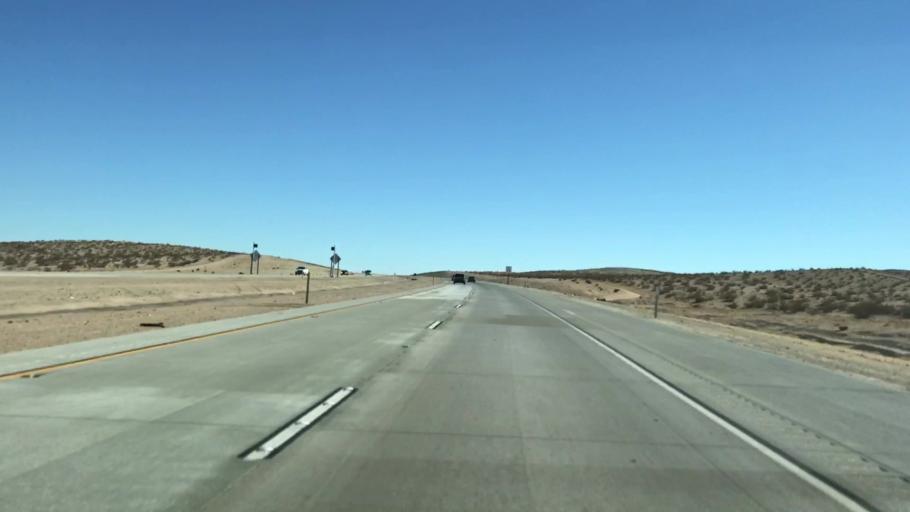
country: US
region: California
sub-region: San Bernardino County
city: Lenwood
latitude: 34.9170
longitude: -117.2424
